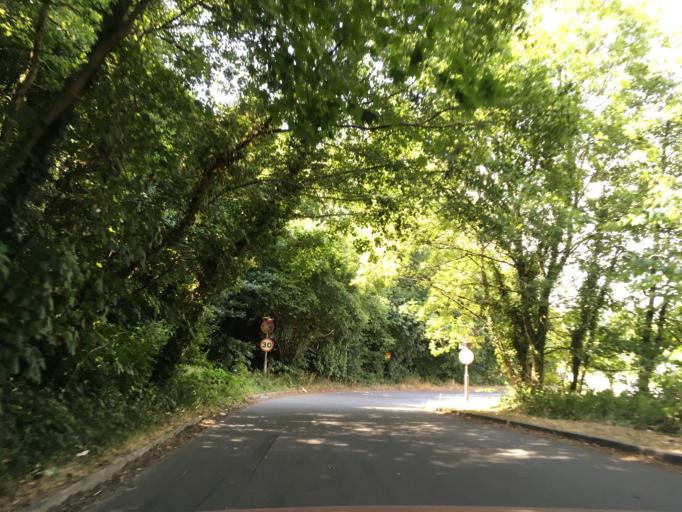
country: GB
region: Wales
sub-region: Caerphilly County Borough
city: Risca
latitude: 51.6000
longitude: -3.0929
